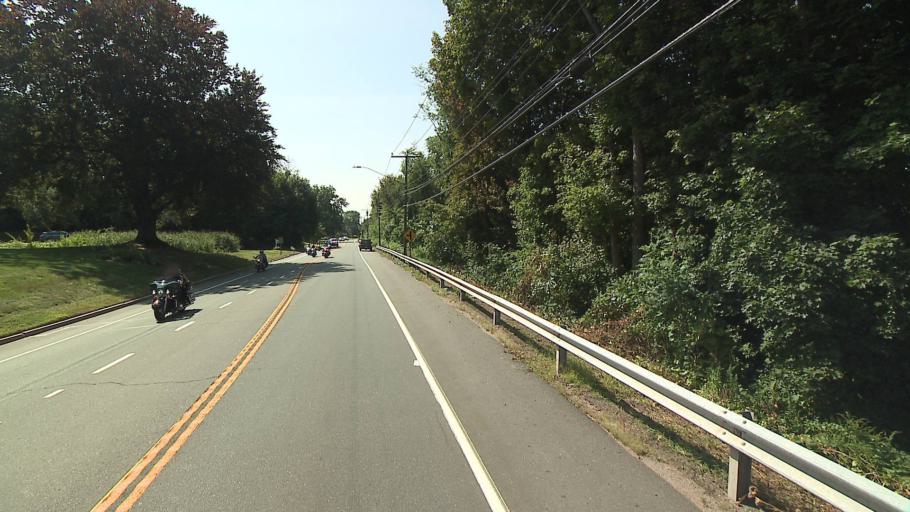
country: US
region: Connecticut
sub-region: Hartford County
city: Windsor Locks
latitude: 41.9257
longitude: -72.6063
